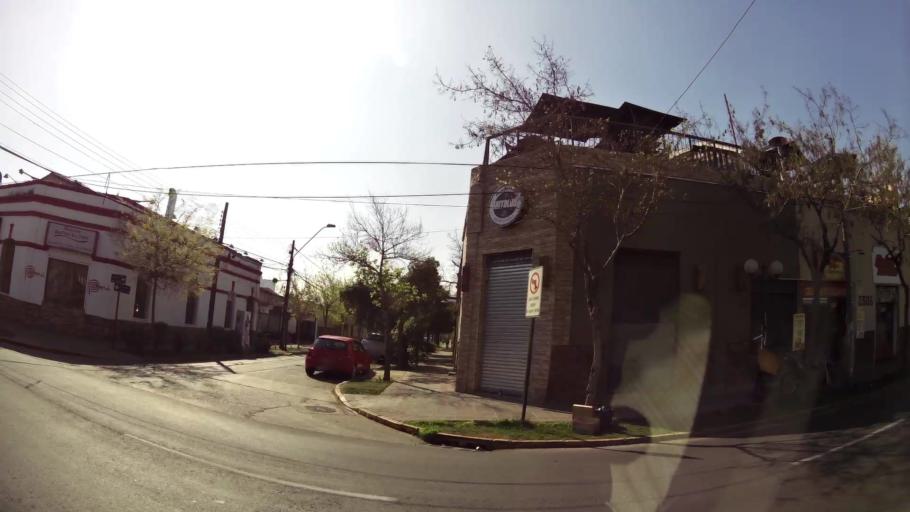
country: CL
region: Santiago Metropolitan
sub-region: Provincia de Santiago
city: Santiago
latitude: -33.4461
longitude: -70.6241
